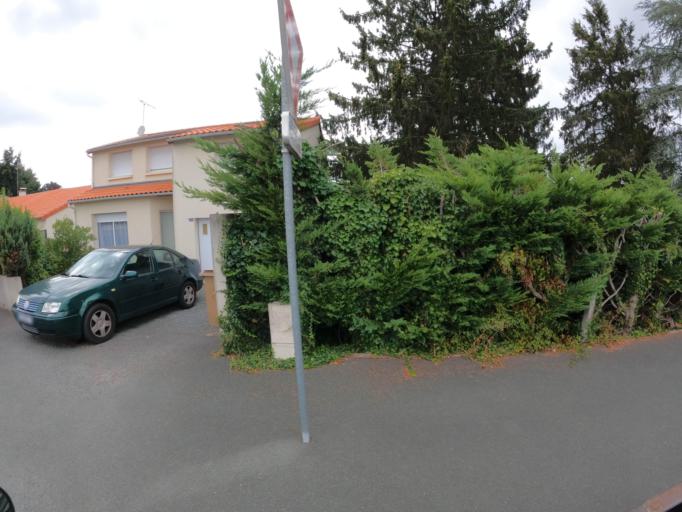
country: FR
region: Pays de la Loire
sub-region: Departement de Maine-et-Loire
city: Cholet
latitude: 47.0511
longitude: -0.9038
